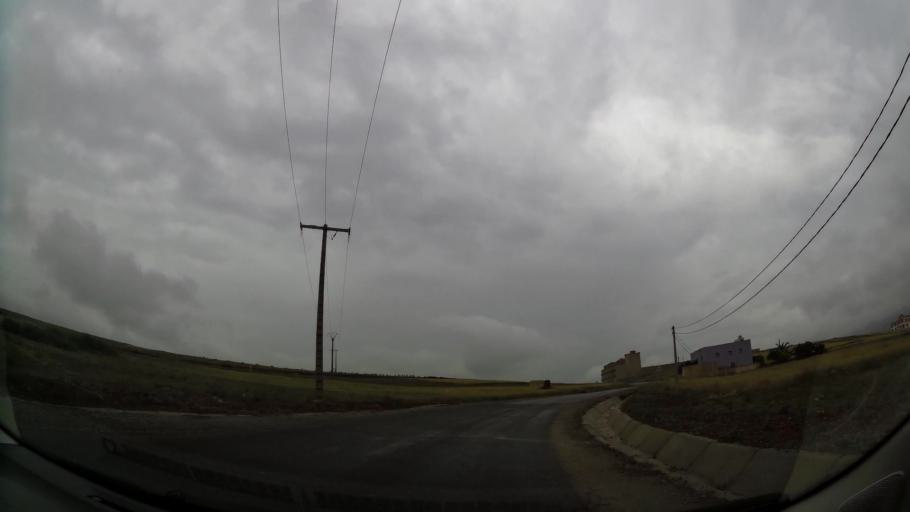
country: MA
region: Oriental
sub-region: Nador
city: Nador
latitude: 35.1519
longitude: -3.0325
